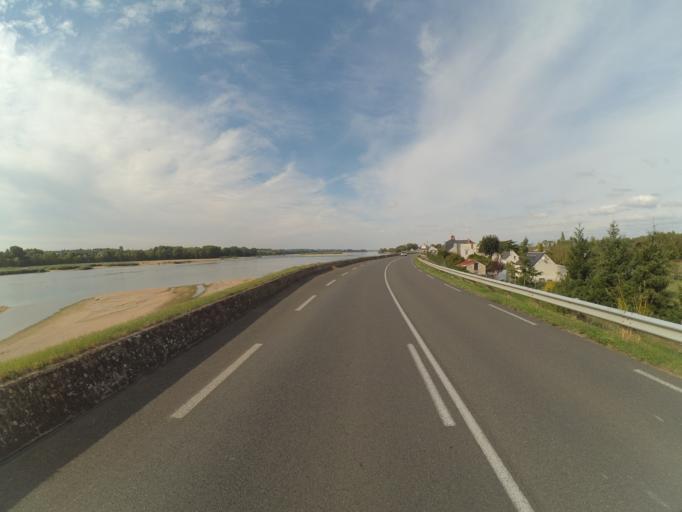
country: FR
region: Pays de la Loire
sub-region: Departement de Maine-et-Loire
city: Varennes-sur-Loire
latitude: 47.2300
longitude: 0.0420
